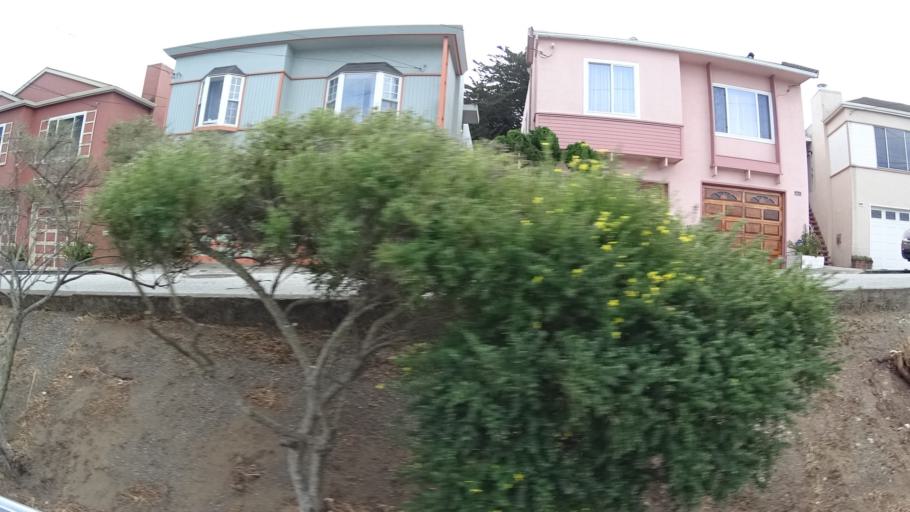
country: US
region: California
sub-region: San Mateo County
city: Daly City
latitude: 37.7095
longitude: -122.4381
